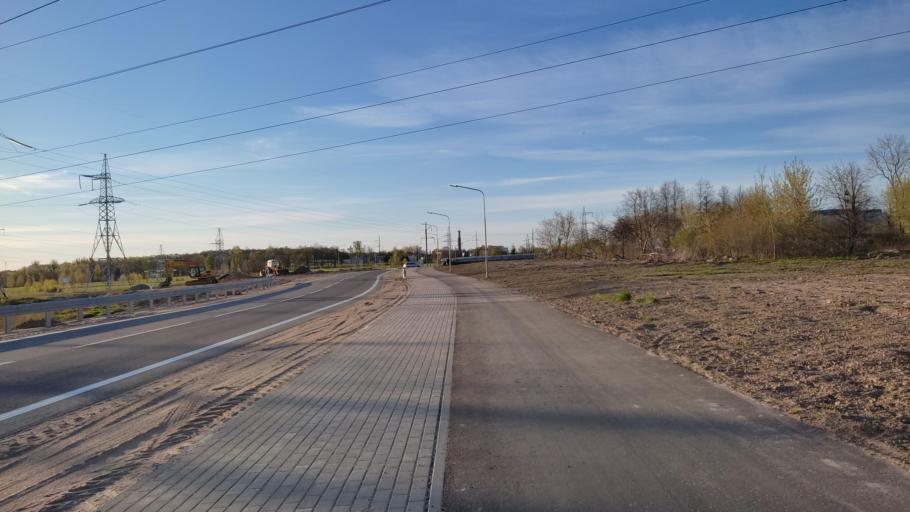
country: BY
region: Grodnenskaya
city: Hrodna
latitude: 53.6676
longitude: 23.8913
